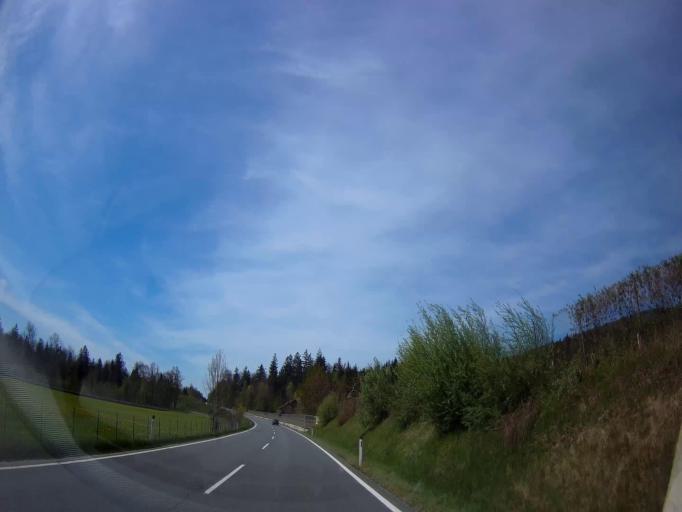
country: AT
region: Salzburg
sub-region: Politischer Bezirk Salzburg-Umgebung
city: Anthering
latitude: 47.8980
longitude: 12.9884
